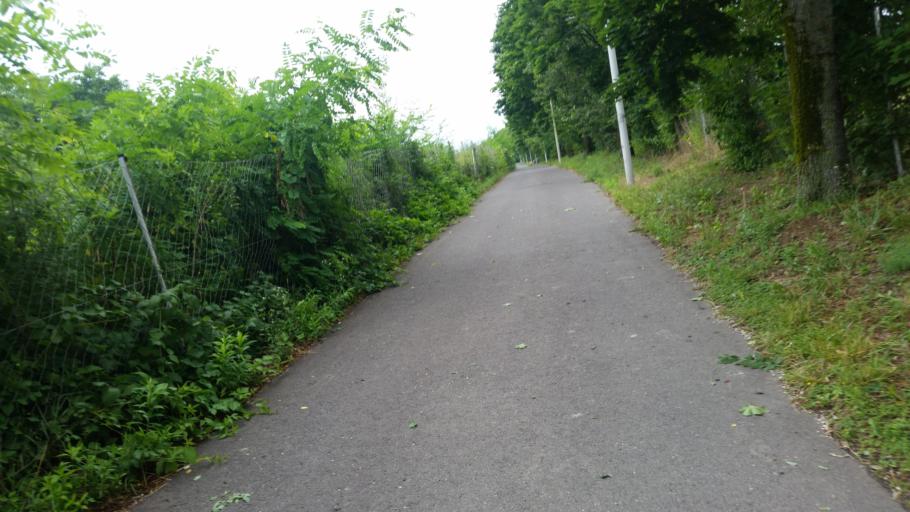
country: AT
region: Upper Austria
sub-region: Politischer Bezirk Linz-Land
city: Leonding
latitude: 48.2600
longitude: 14.2769
